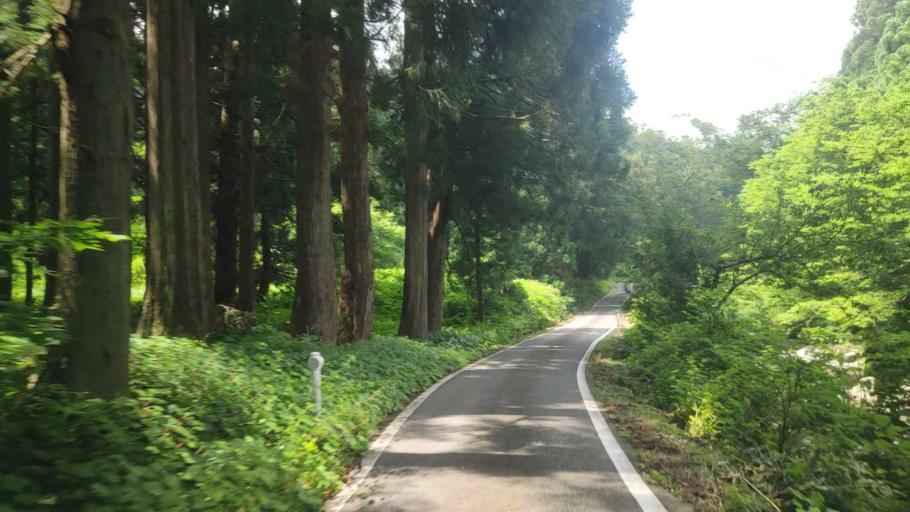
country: JP
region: Fukui
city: Katsuyama
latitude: 36.1918
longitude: 136.5262
